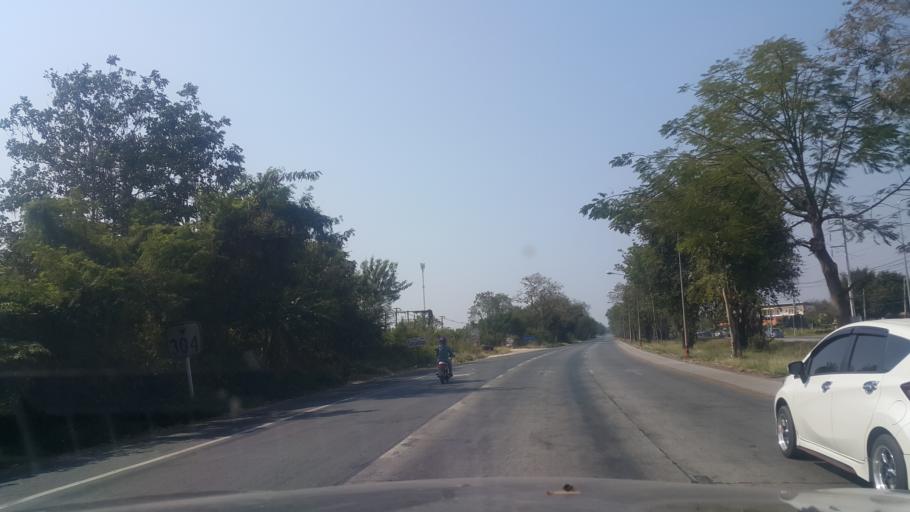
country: TH
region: Nakhon Ratchasima
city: Pak Thong Chai
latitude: 14.7415
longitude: 102.0317
